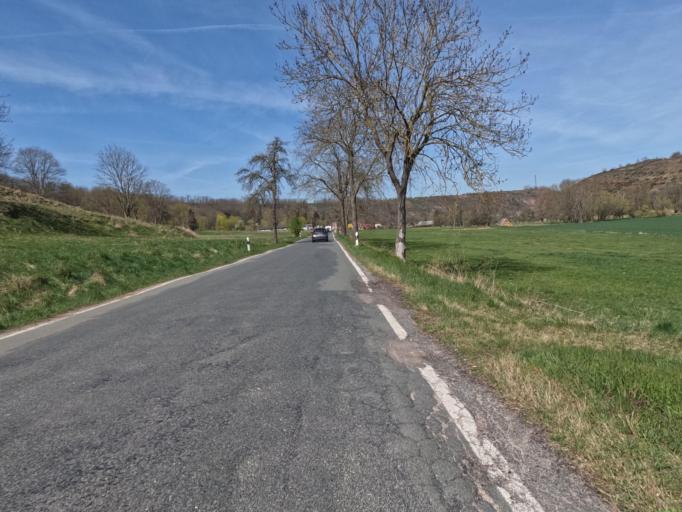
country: DE
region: Saxony-Anhalt
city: Konnern
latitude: 51.6353
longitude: 11.7501
